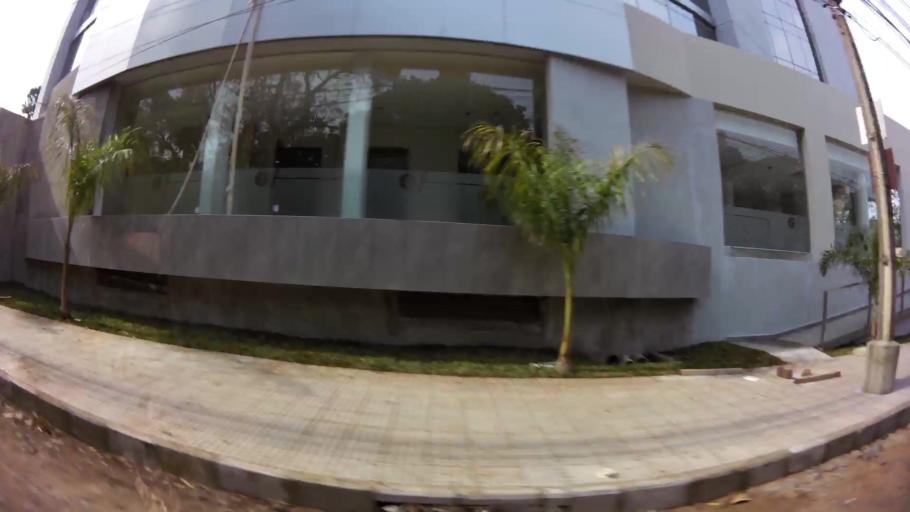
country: PY
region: Central
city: Fernando de la Mora
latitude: -25.2819
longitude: -57.5642
